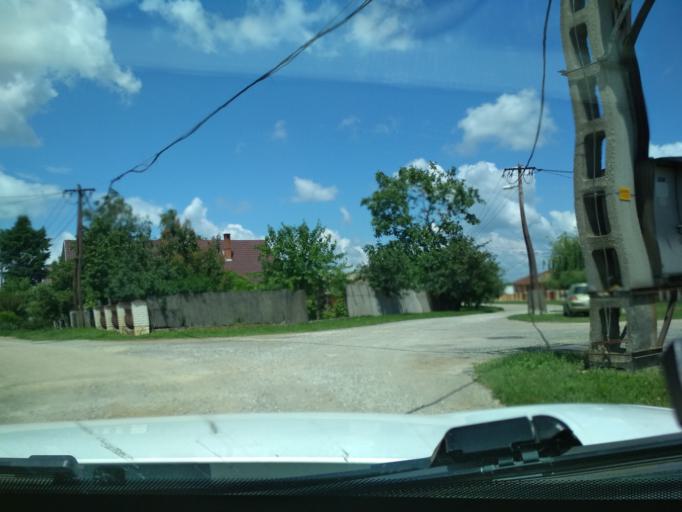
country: HU
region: Jasz-Nagykun-Szolnok
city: Tiszafured
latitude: 47.6017
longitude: 20.7589
